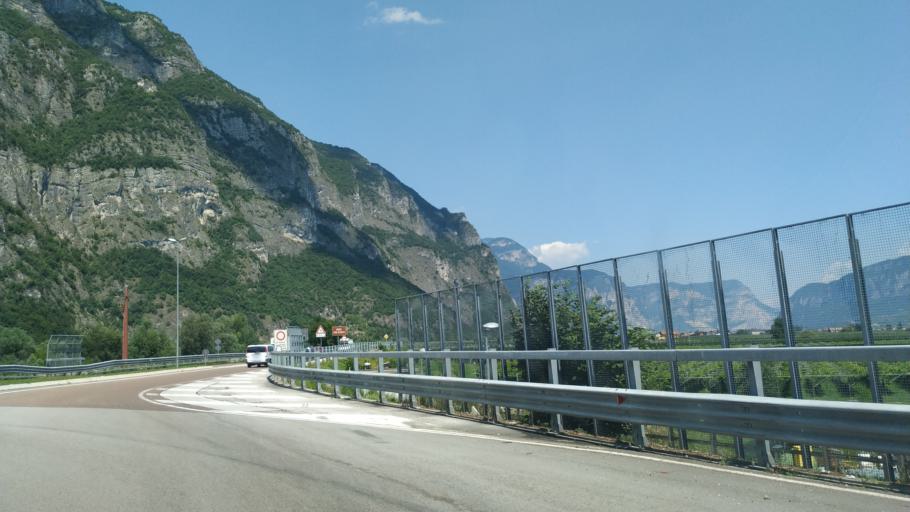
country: IT
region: Trentino-Alto Adige
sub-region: Provincia di Trento
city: Zambana
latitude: 46.1567
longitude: 11.0787
